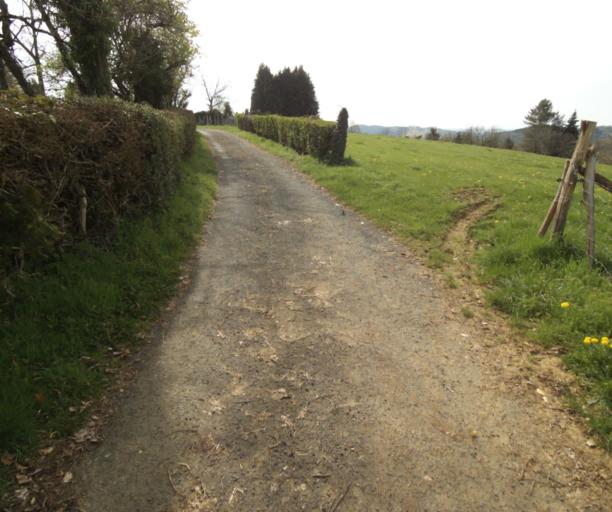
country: FR
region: Limousin
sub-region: Departement de la Correze
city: Correze
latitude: 45.3562
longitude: 1.8140
